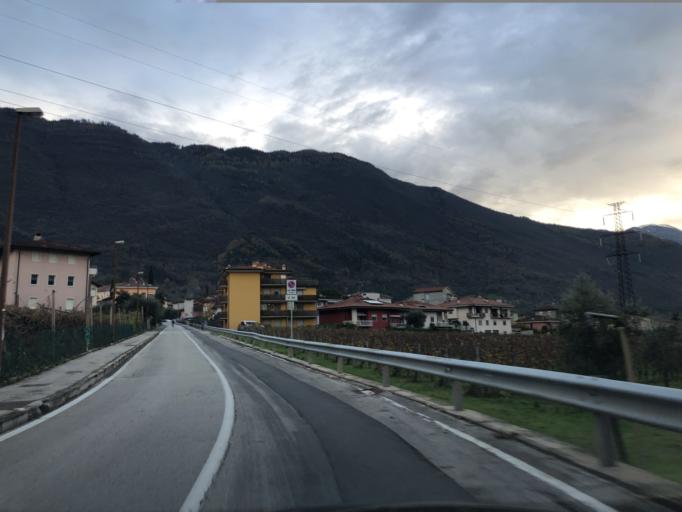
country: IT
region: Trentino-Alto Adige
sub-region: Provincia di Trento
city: Bolognano-Vignole
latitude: 45.9152
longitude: 10.9008
